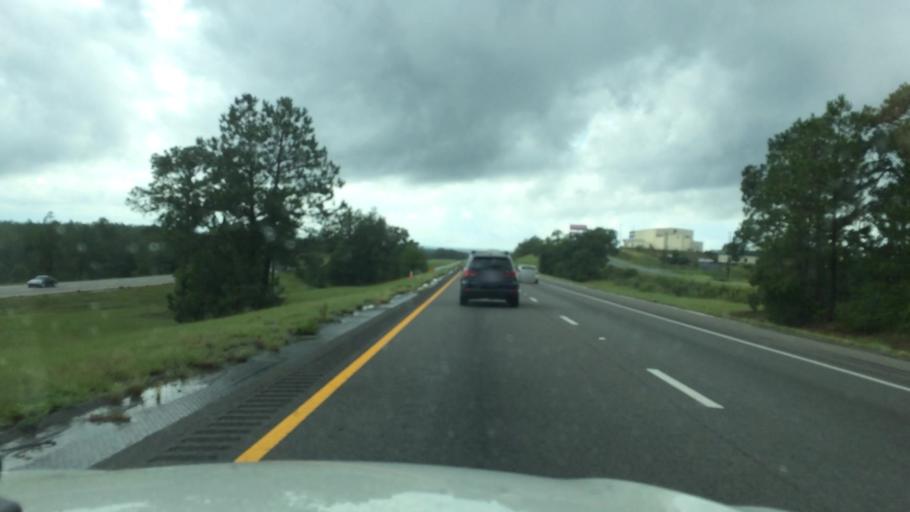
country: US
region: South Carolina
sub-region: Kershaw County
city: Elgin
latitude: 34.1621
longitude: -80.7234
